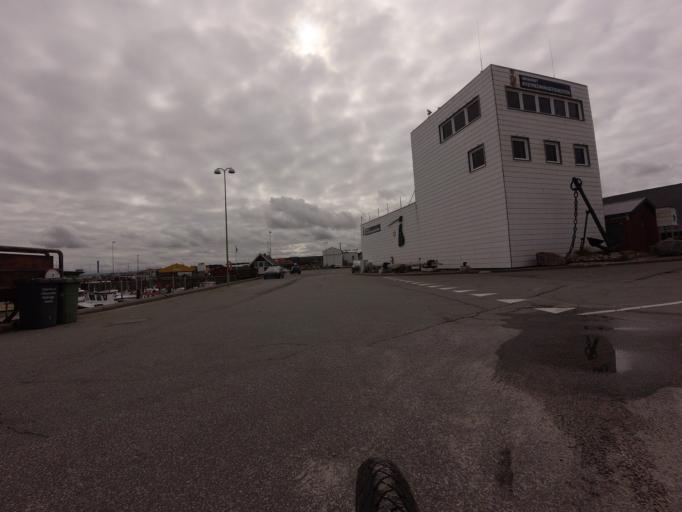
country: DK
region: North Denmark
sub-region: Hjorring Kommune
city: Hirtshals
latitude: 57.5949
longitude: 9.9584
